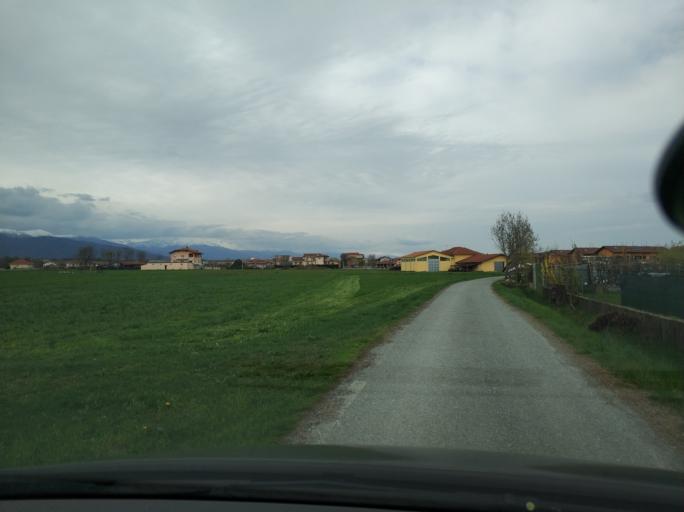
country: IT
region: Piedmont
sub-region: Provincia di Torino
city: Nole
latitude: 45.2346
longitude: 7.5632
